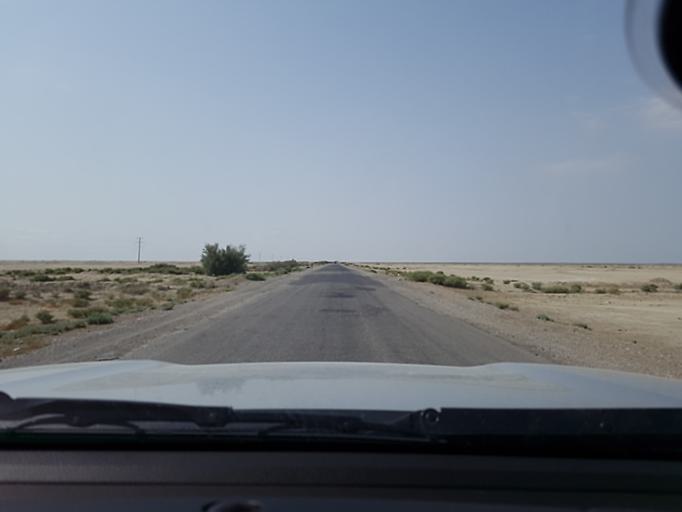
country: TM
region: Balkan
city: Gumdag
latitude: 38.9820
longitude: 54.5873
